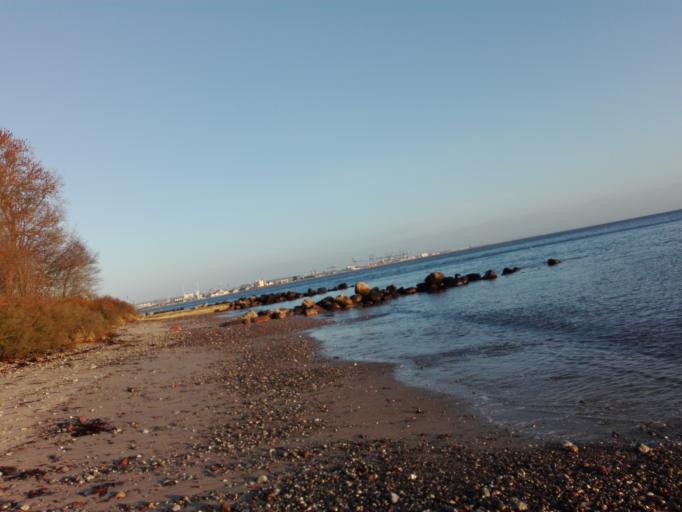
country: DK
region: Central Jutland
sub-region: Arhus Kommune
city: Arhus
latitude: 56.1190
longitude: 10.2281
